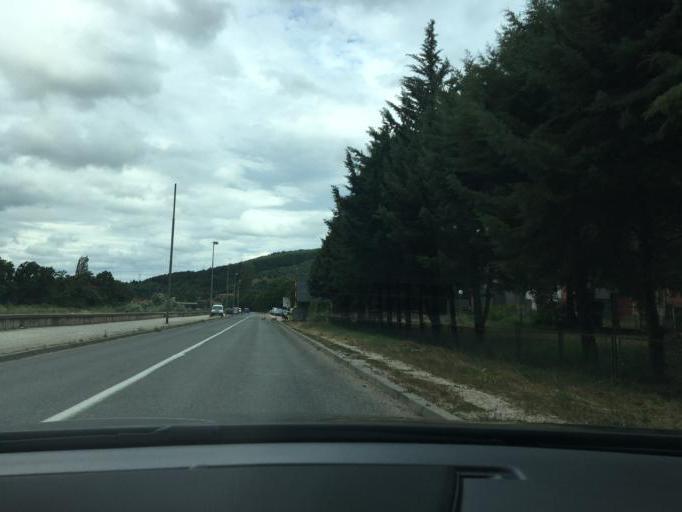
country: MK
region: Kriva Palanka
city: Kriva Palanka
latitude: 42.2006
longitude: 22.3306
